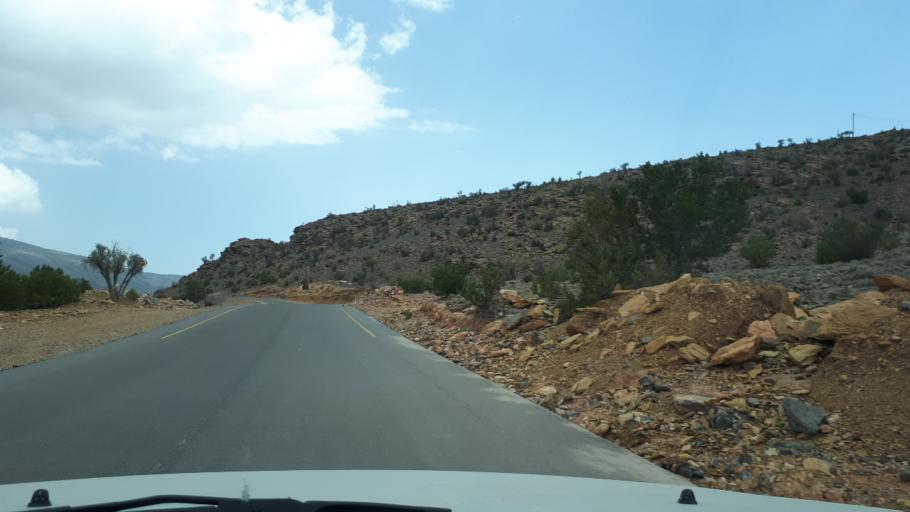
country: OM
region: Muhafazat ad Dakhiliyah
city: Bahla'
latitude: 23.2253
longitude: 57.2023
